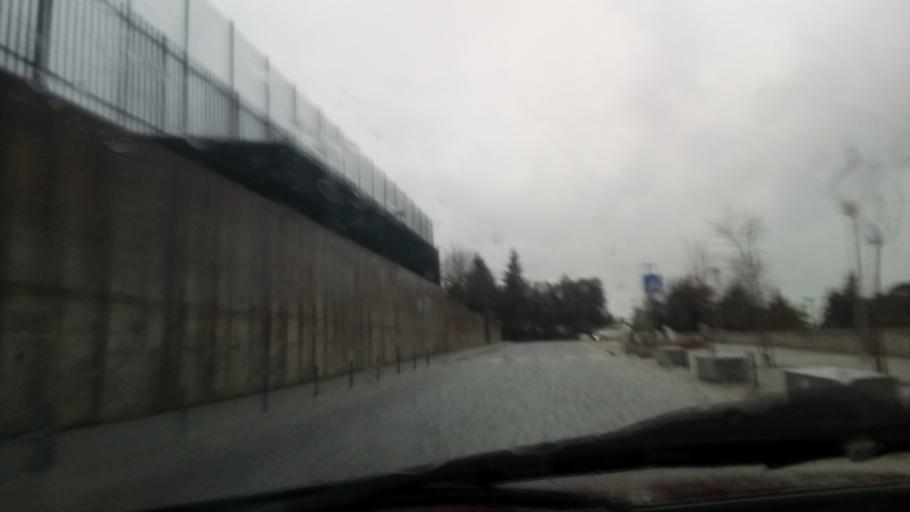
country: PT
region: Guarda
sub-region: Celorico da Beira
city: Celorico da Beira
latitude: 40.6324
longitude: -7.3961
